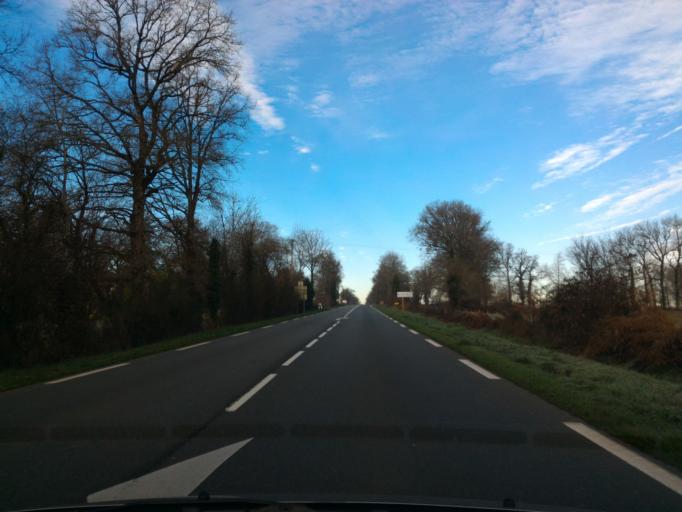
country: FR
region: Poitou-Charentes
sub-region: Departement de la Charente
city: Confolens
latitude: 46.0299
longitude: 0.6445
